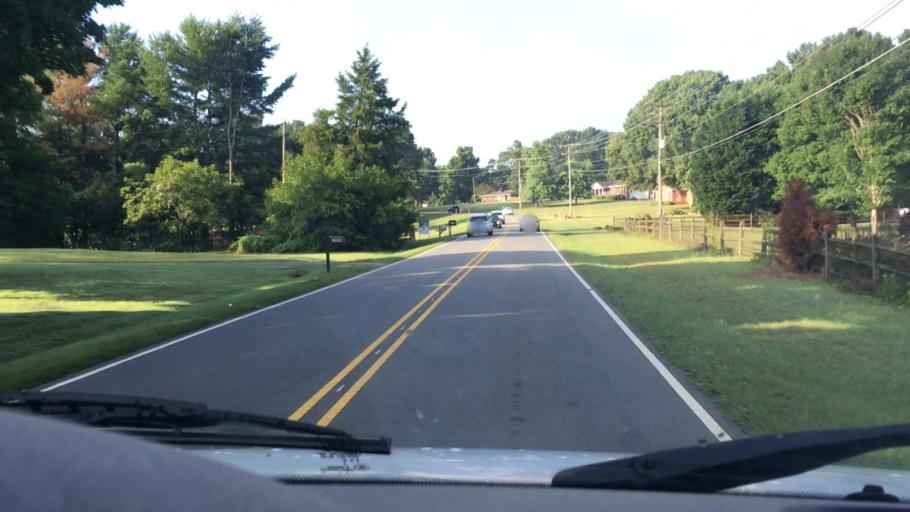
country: US
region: North Carolina
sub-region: Mecklenburg County
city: Huntersville
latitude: 35.4100
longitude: -80.9259
